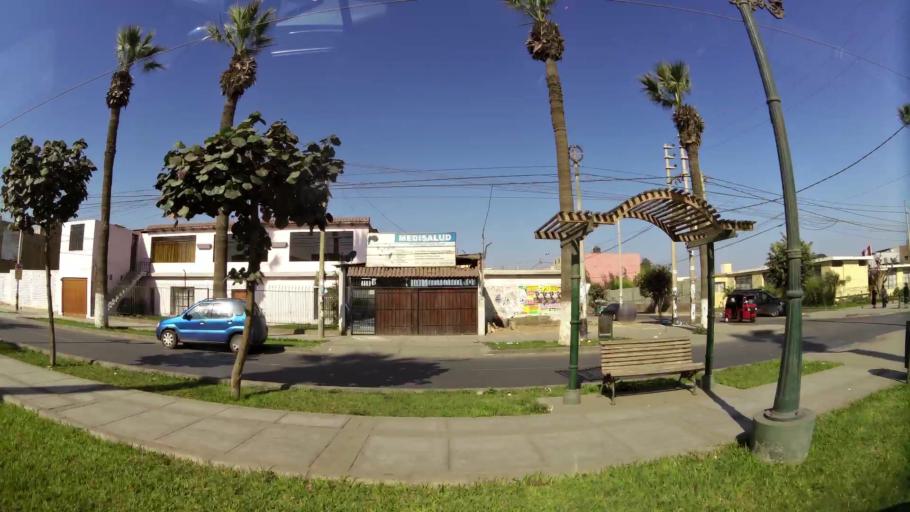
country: PE
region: Ica
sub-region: Provincia de Chincha
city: Chincha Alta
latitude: -13.4113
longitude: -76.1315
